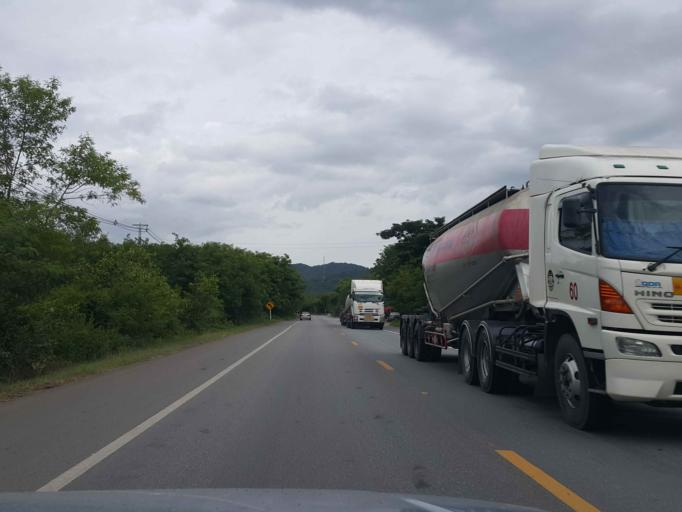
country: TH
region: Lampang
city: Lampang
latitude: 18.2511
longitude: 99.5317
